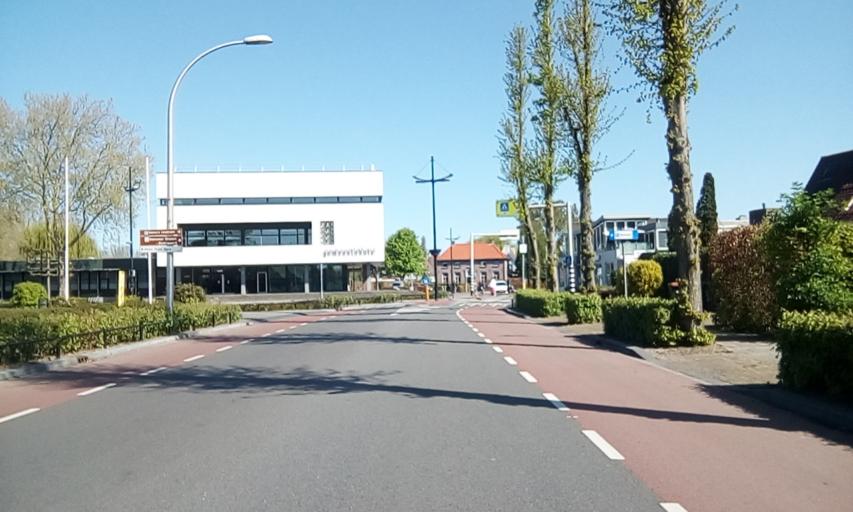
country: NL
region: Gelderland
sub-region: Gemeente Druten
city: Druten
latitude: 51.8876
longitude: 5.6051
